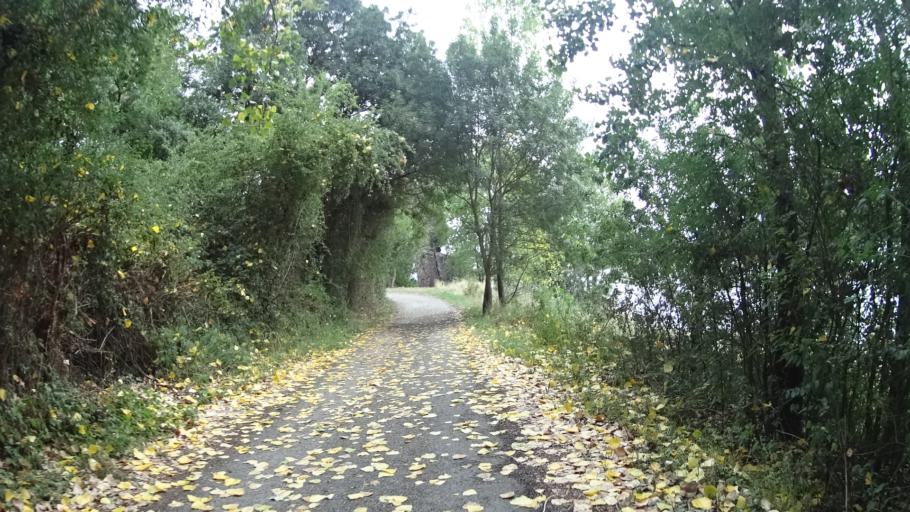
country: FR
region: Pays de la Loire
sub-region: Departement de Maine-et-Loire
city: Denee
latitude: 47.3957
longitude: -0.6291
